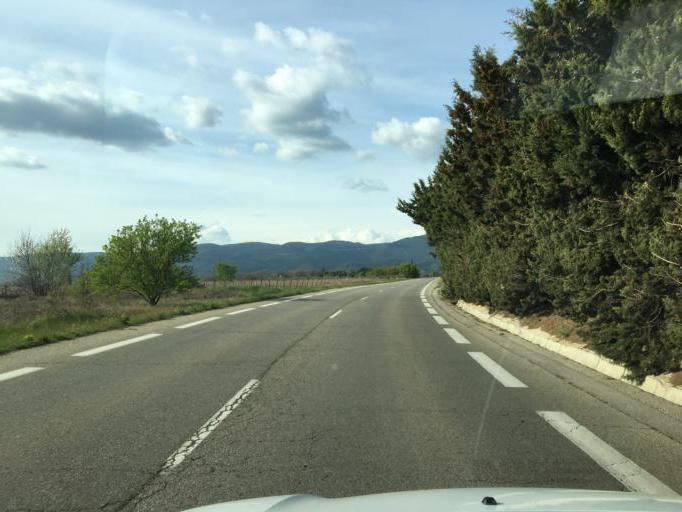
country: FR
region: Provence-Alpes-Cote d'Azur
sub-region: Departement du Vaucluse
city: Ansouis
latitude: 43.7468
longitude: 5.4623
